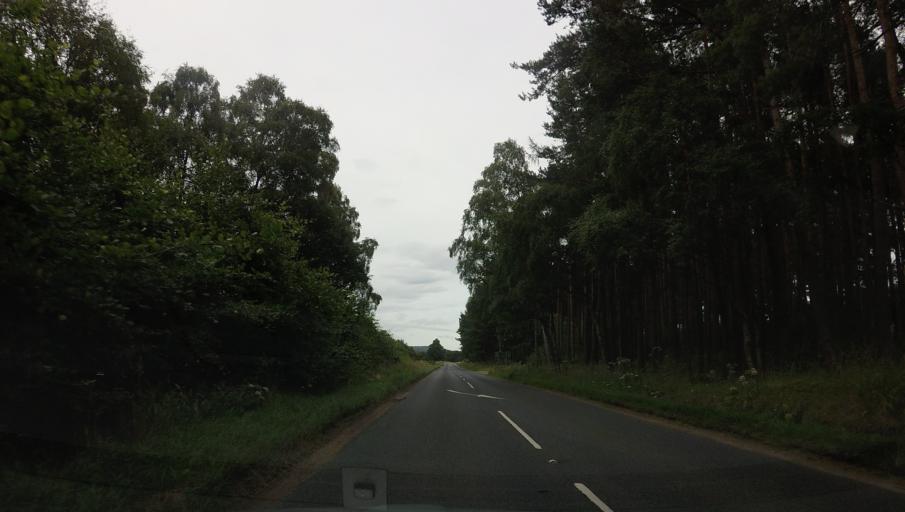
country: GB
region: Scotland
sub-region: Aberdeenshire
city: Aboyne
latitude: 57.0887
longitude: -2.7479
